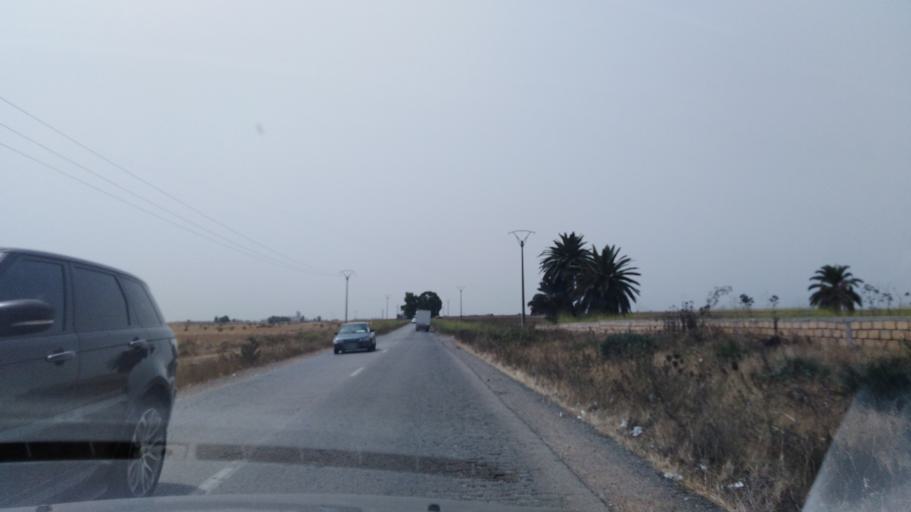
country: MA
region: Grand Casablanca
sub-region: Nouaceur
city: Dar Bouazza
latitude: 33.4107
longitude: -7.8084
